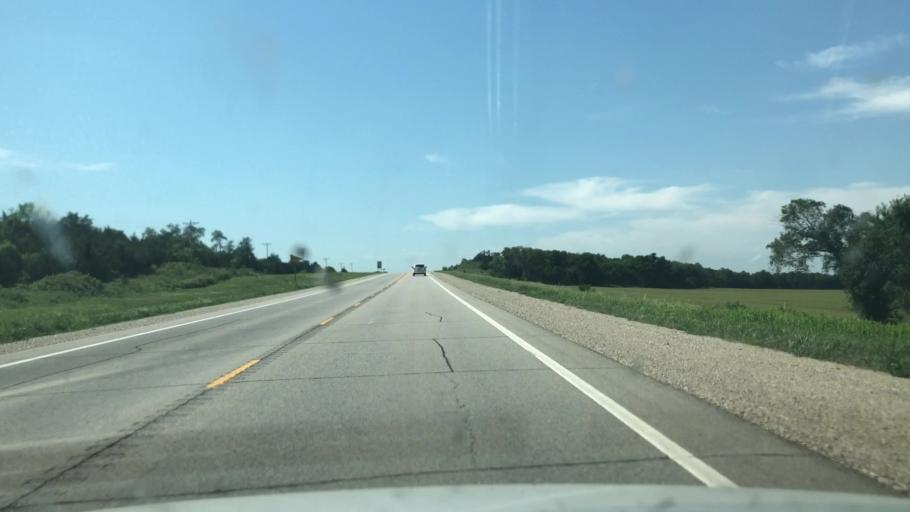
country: US
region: Kansas
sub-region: Cowley County
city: Winfield
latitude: 37.3747
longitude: -97.0071
